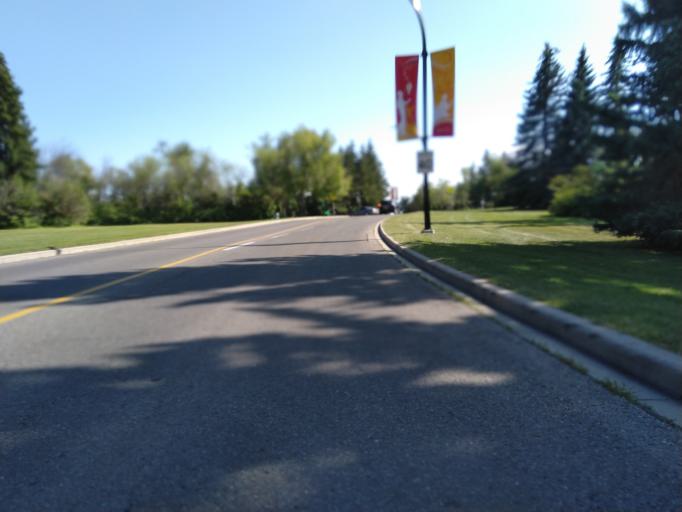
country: CA
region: Alberta
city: Calgary
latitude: 51.0778
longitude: -114.1234
